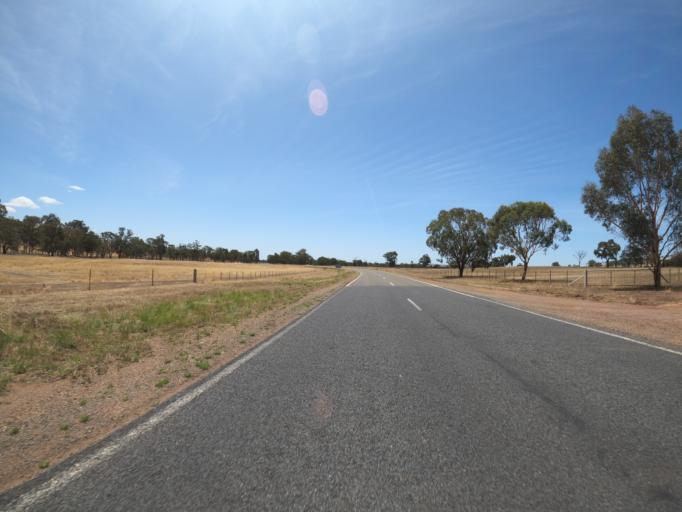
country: AU
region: Victoria
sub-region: Benalla
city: Benalla
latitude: -36.3315
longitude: 145.9610
